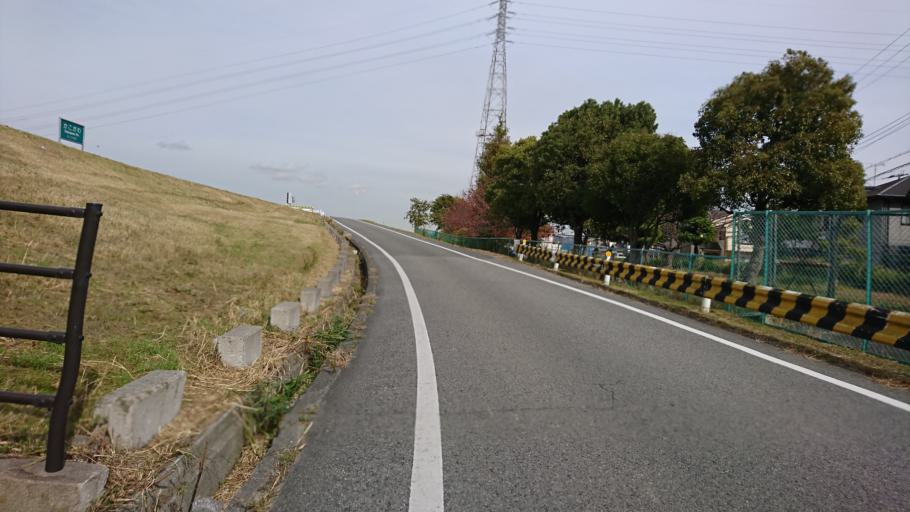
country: JP
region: Hyogo
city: Kakogawacho-honmachi
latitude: 34.7643
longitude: 134.8122
